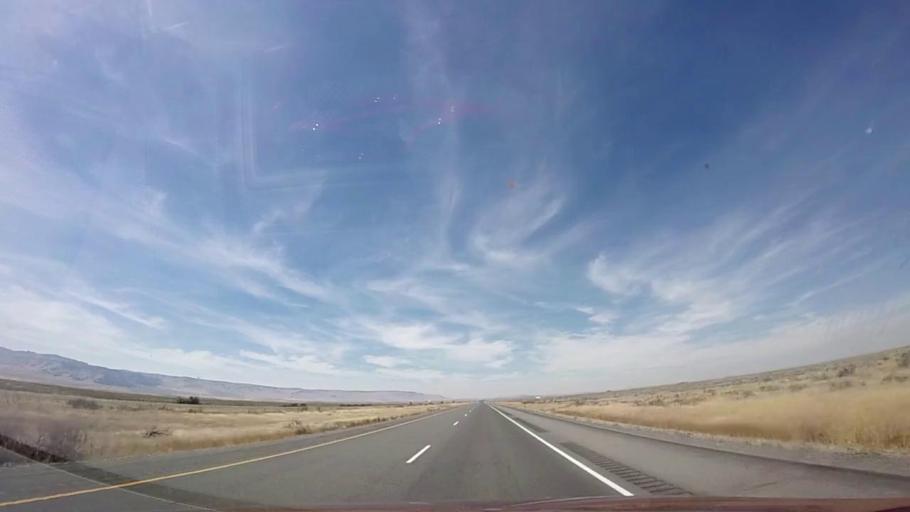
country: US
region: Idaho
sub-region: Minidoka County
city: Rupert
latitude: 42.3740
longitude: -113.2707
